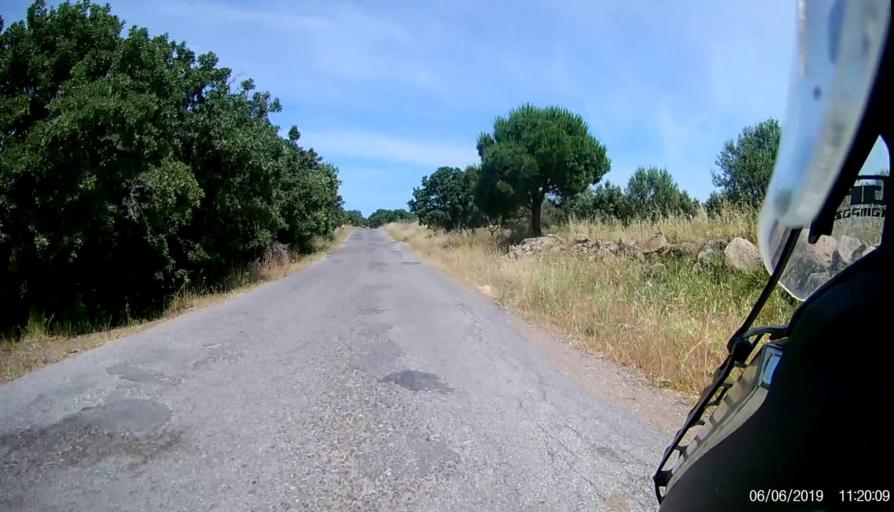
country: TR
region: Canakkale
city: Gulpinar
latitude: 39.6635
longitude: 26.1638
